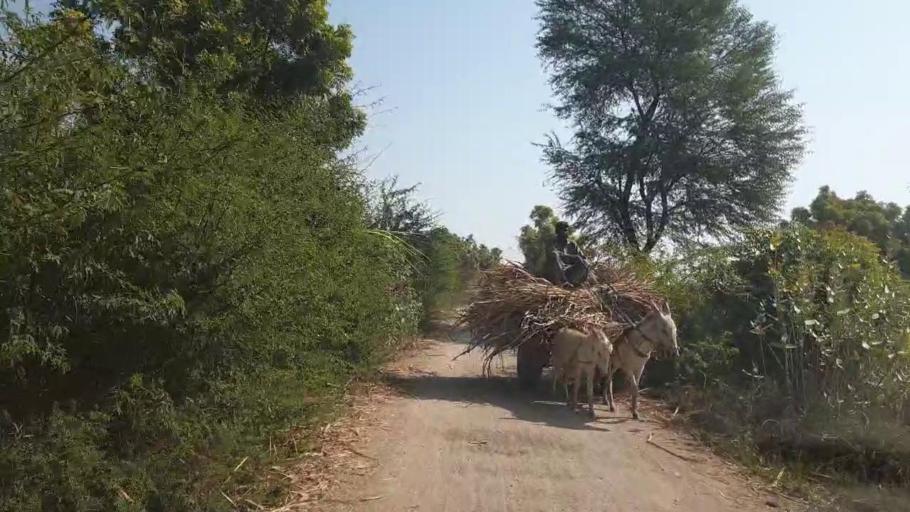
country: PK
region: Sindh
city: Tando Adam
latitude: 25.6268
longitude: 68.7409
